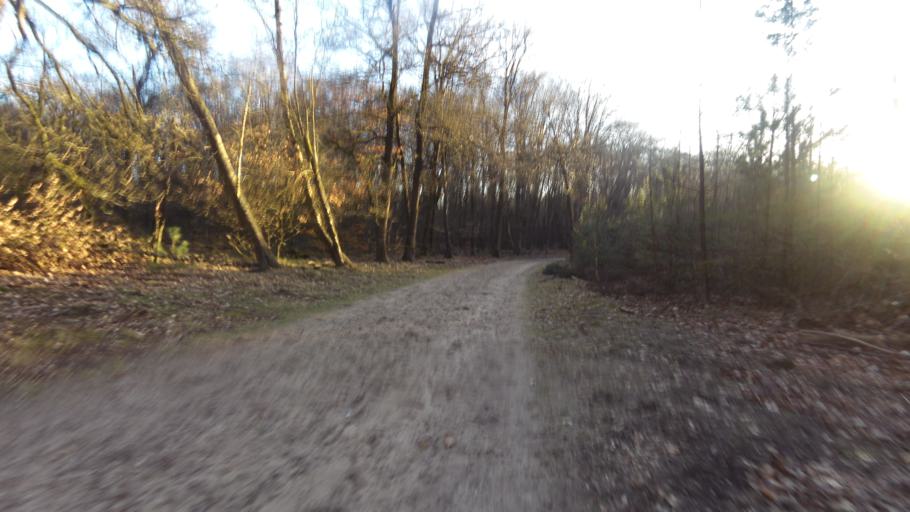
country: NL
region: Gelderland
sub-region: Gemeente Putten
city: Putten
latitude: 52.2494
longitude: 5.6554
